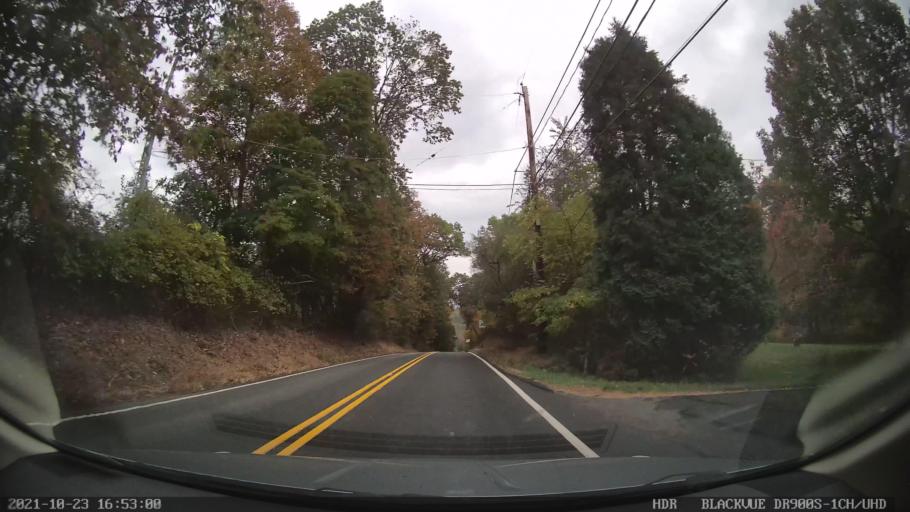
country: US
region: Pennsylvania
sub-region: Berks County
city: Red Lion
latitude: 40.4606
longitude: -75.5920
